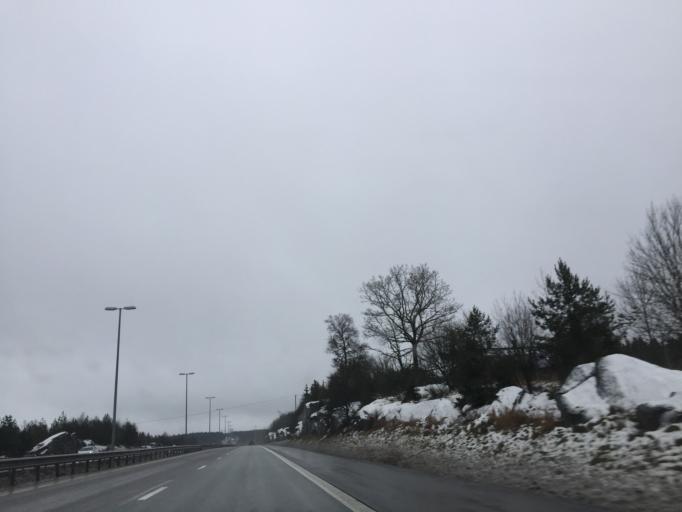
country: NO
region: Akershus
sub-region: Vestby
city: Vestby
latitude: 59.5500
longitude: 10.7227
